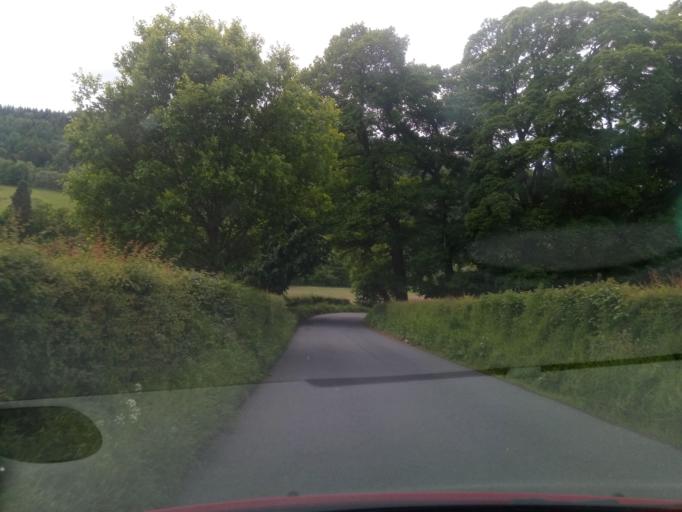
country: GB
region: Scotland
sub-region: The Scottish Borders
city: Selkirk
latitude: 55.5849
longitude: -2.8525
